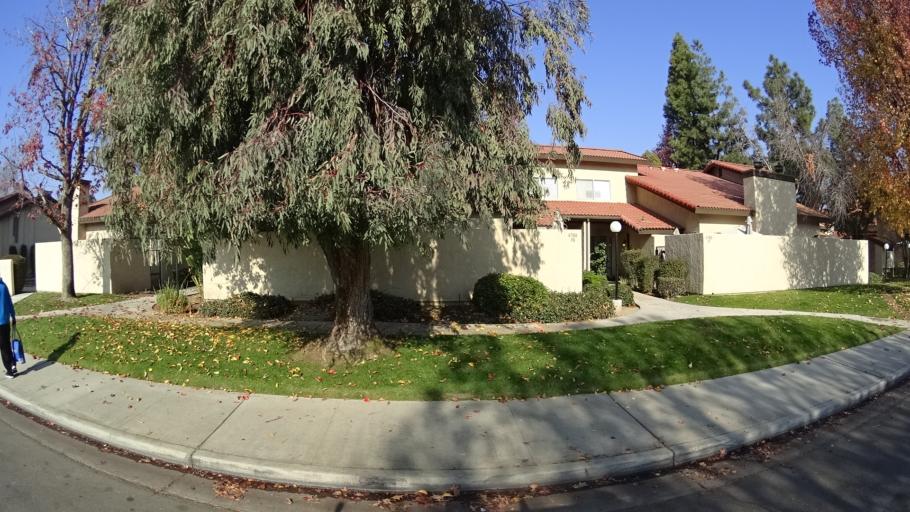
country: US
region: California
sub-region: Kern County
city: Greenacres
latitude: 35.3328
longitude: -119.0762
